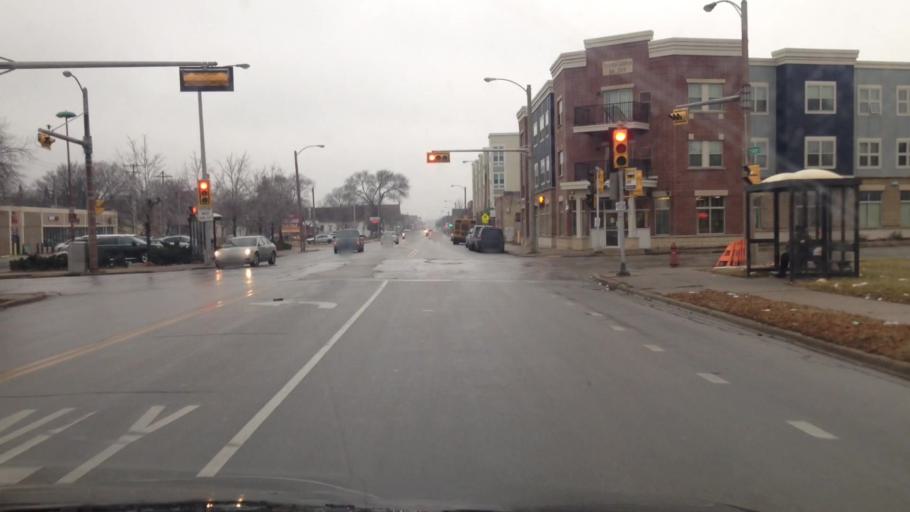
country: US
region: Wisconsin
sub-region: Milwaukee County
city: Milwaukee
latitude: 43.0677
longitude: -87.9287
